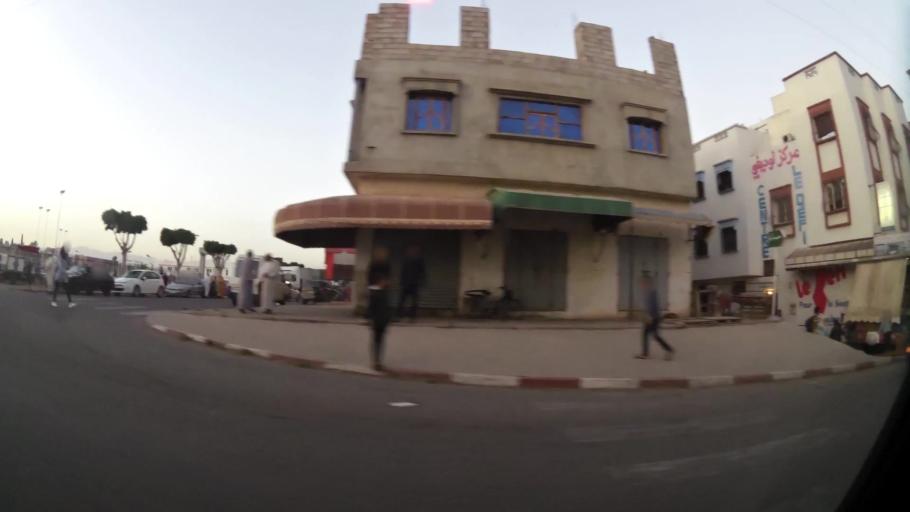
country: MA
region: Souss-Massa-Draa
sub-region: Inezgane-Ait Mellou
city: Inezgane
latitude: 30.3759
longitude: -9.4950
